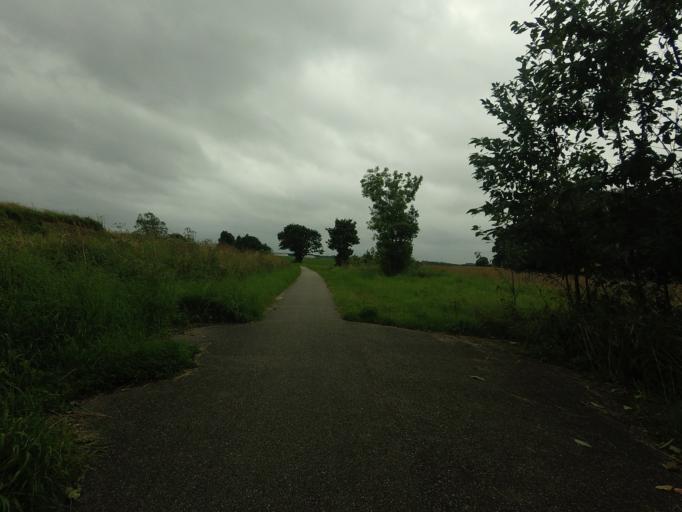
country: DK
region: Central Jutland
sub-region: Horsens Kommune
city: Braedstrup
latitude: 55.9915
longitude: 9.5891
